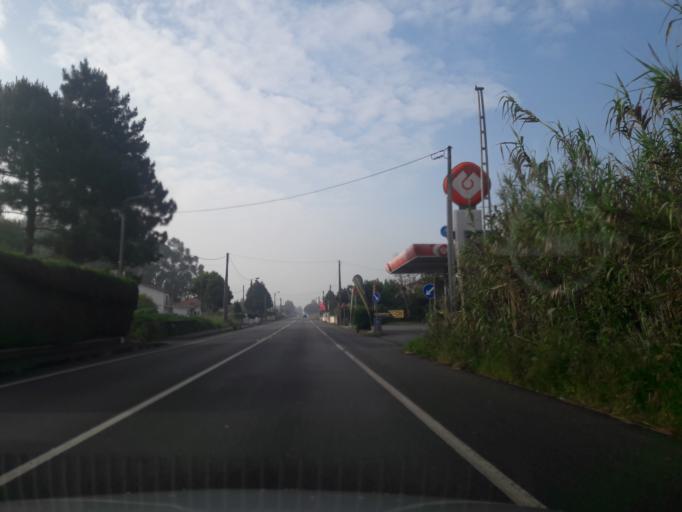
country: PT
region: Porto
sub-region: Vila do Conde
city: Arvore
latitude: 41.3136
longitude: -8.7081
